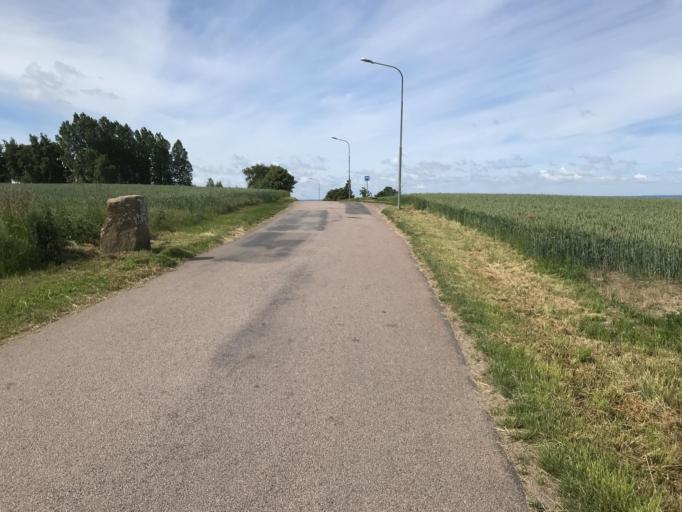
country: SE
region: Skane
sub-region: Helsingborg
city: Glumslov
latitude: 55.9351
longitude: 12.8016
